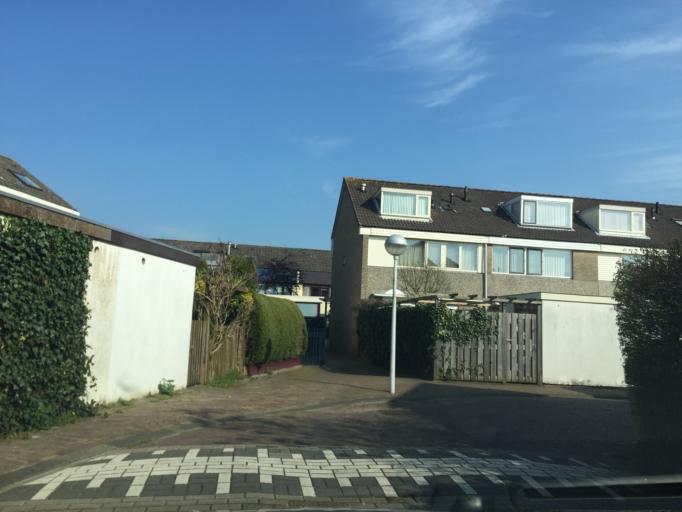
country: NL
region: South Holland
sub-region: Gemeente Leiden
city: Leiden
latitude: 52.1823
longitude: 4.5078
